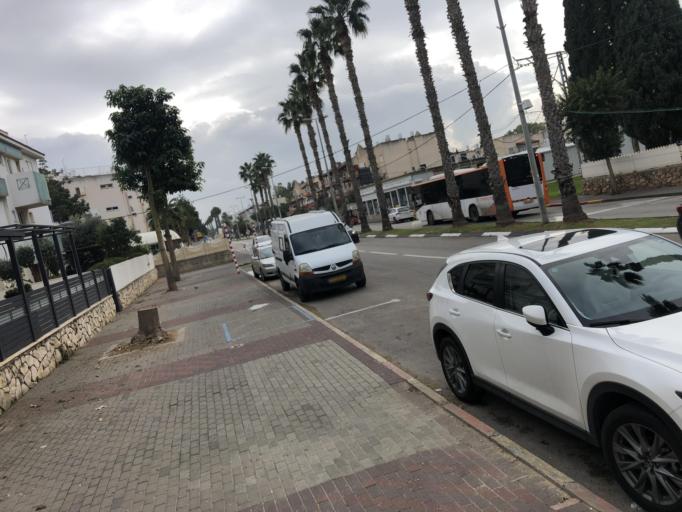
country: IL
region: Northern District
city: `Akko
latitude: 32.9298
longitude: 35.0927
